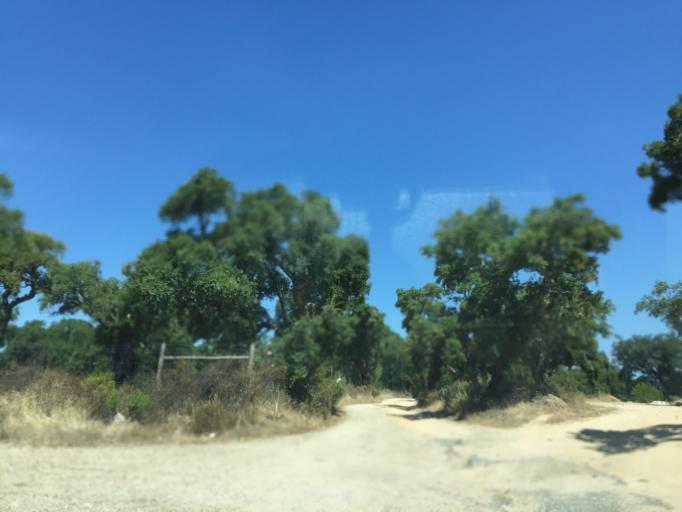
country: PT
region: Lisbon
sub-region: Alenquer
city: Carregado
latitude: 39.0529
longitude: -8.9264
